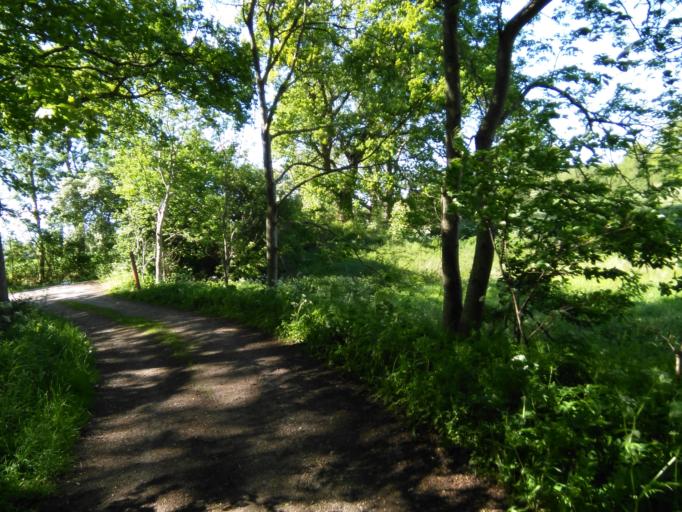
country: DK
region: Central Jutland
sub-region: Arhus Kommune
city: Marslet
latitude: 56.0259
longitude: 10.1538
